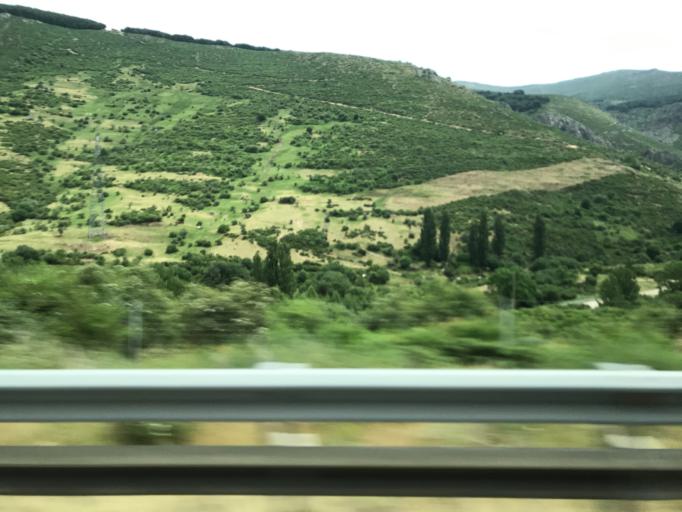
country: ES
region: Madrid
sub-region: Provincia de Madrid
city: Somosierra
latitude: 41.1486
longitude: -3.5837
